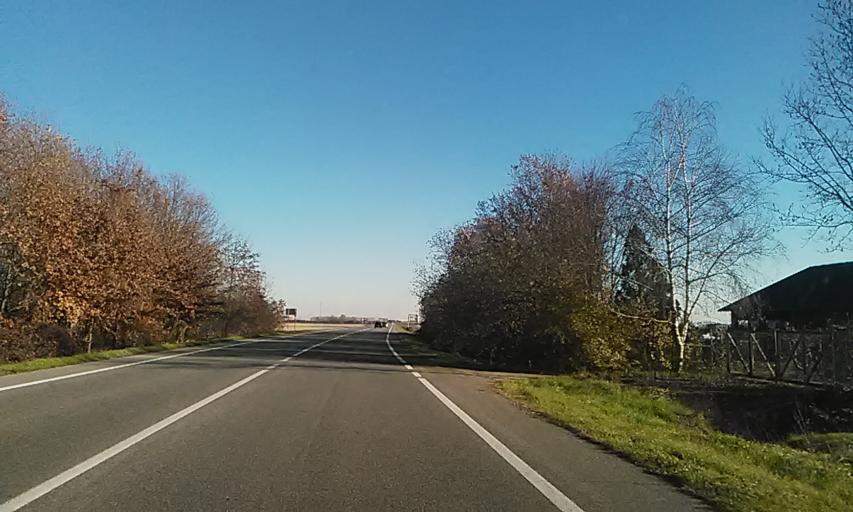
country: IT
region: Piedmont
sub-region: Provincia di Vercelli
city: Vercelli
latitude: 45.3003
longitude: 8.4273
